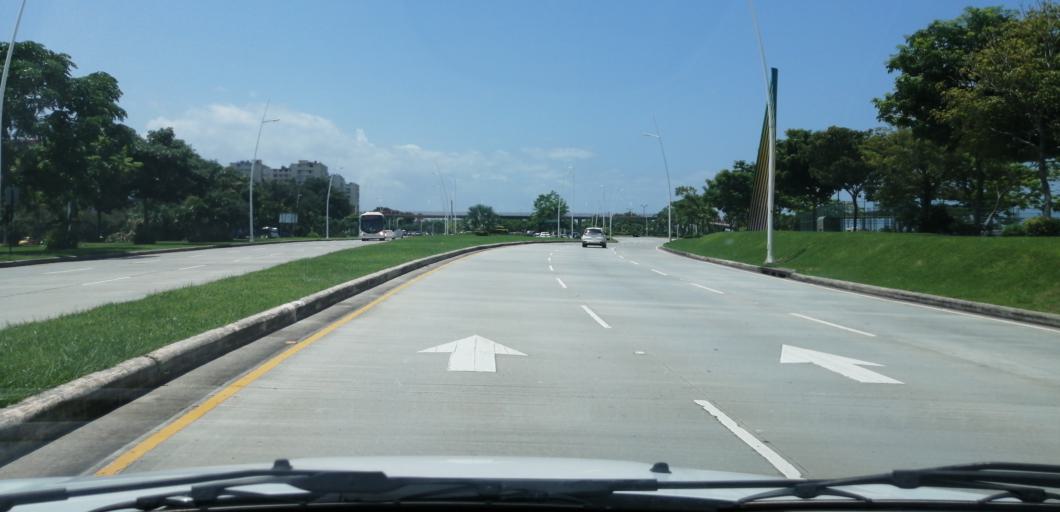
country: PA
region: Panama
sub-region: Distrito de Panama
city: Ancon
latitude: 8.9480
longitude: -79.5449
